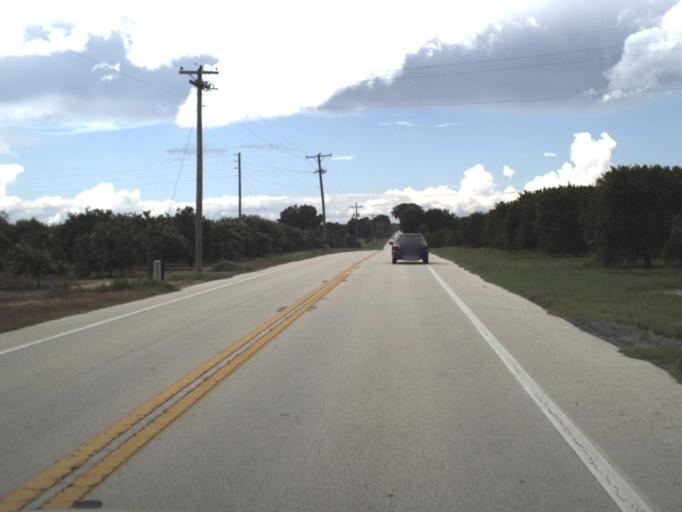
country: US
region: Florida
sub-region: Polk County
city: Fort Meade
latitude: 27.7481
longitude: -81.7350
